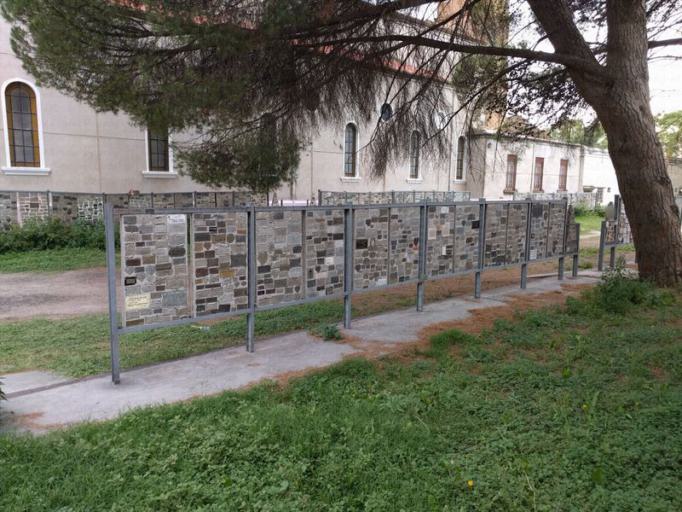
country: AR
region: Buenos Aires
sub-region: Partido de Villarino
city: Medanos
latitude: -39.5245
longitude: -62.6613
